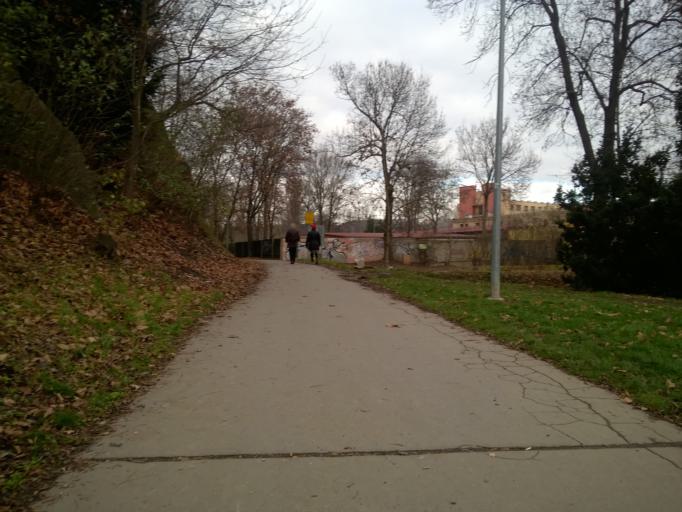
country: CZ
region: Praha
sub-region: Praha 1
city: Mala Strana
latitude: 50.1073
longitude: 14.4067
